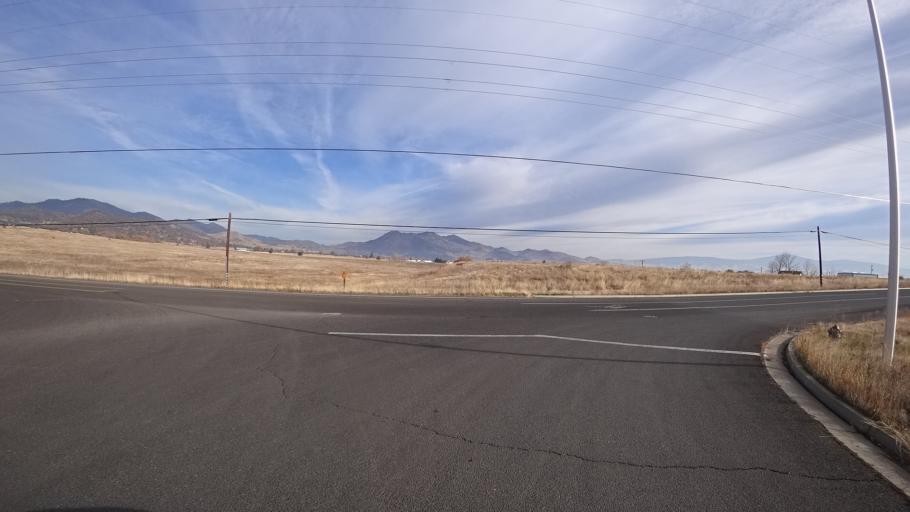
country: US
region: California
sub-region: Siskiyou County
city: Yreka
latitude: 41.7359
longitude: -122.5967
